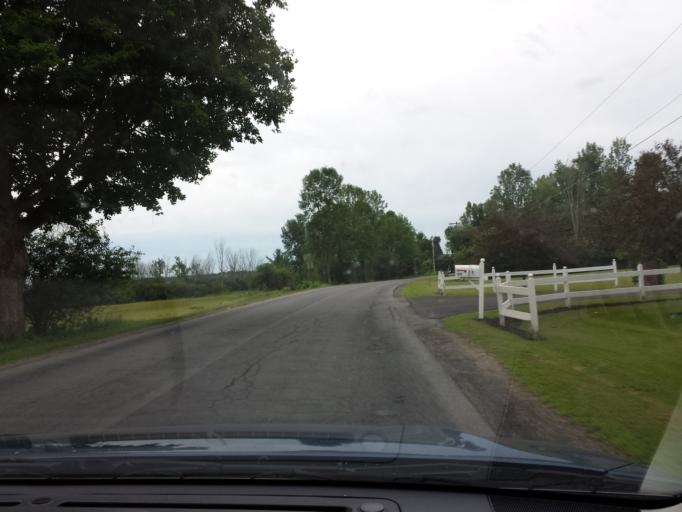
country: US
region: New York
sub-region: St. Lawrence County
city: Potsdam
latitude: 44.6922
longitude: -74.9649
